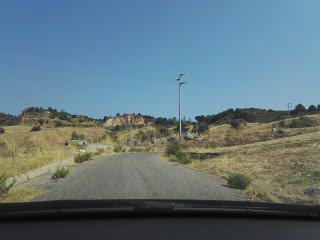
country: IT
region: Calabria
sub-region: Provincia di Reggio Calabria
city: Stignano
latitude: 38.4338
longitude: 16.4609
